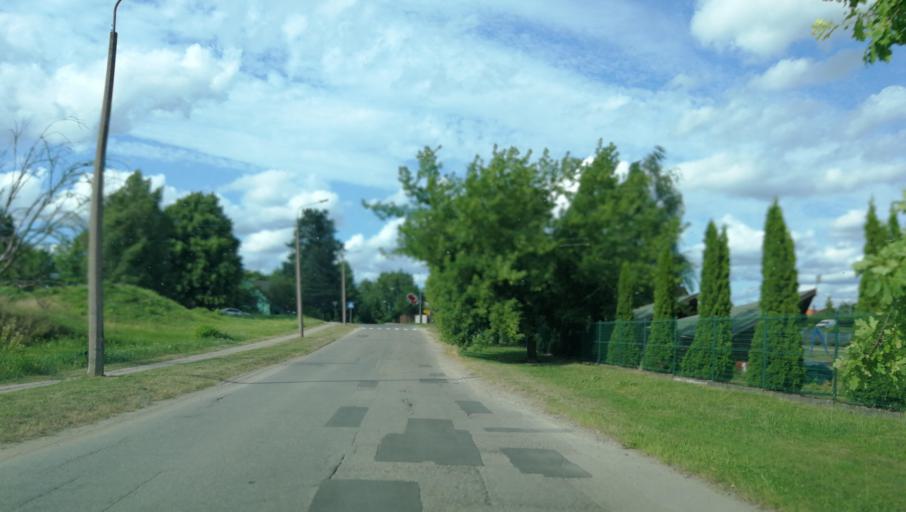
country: LV
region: Cesu Rajons
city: Cesis
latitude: 57.3081
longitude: 25.2893
